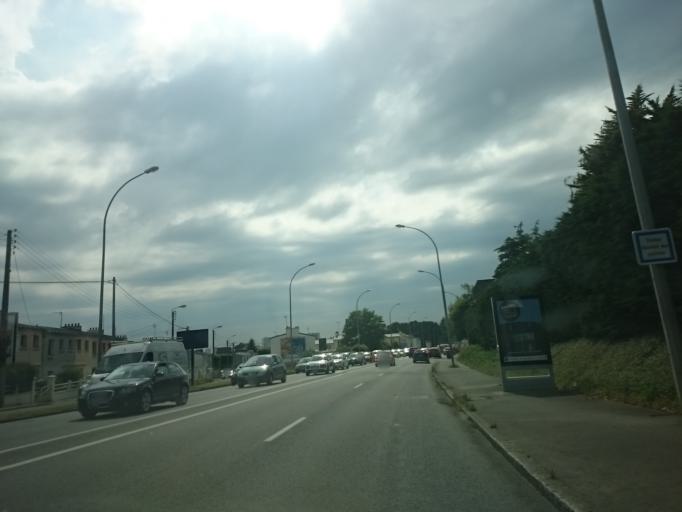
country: FR
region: Brittany
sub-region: Departement du Finistere
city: Brest
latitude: 48.4134
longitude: -4.4846
